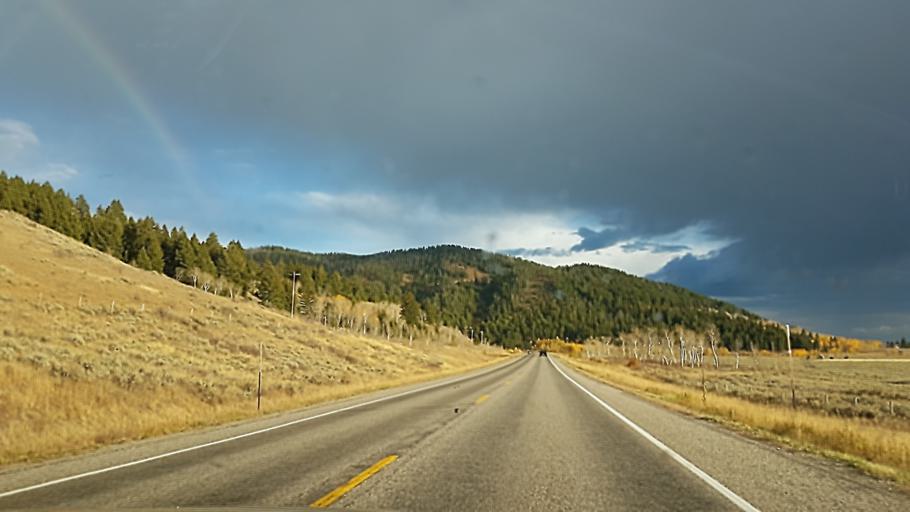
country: US
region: Montana
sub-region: Gallatin County
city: West Yellowstone
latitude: 44.6414
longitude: -111.3361
